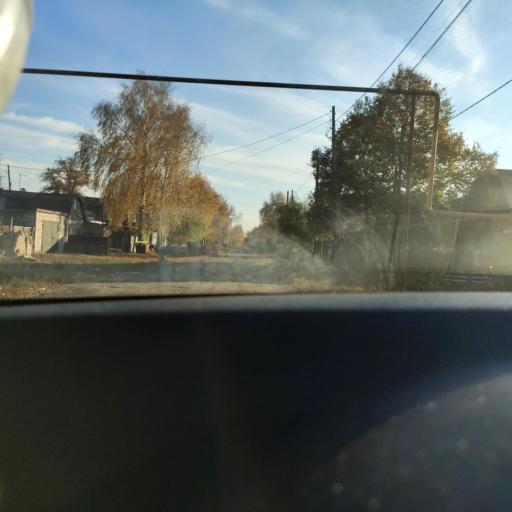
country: RU
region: Samara
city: Petra-Dubrava
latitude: 53.2551
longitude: 50.3242
